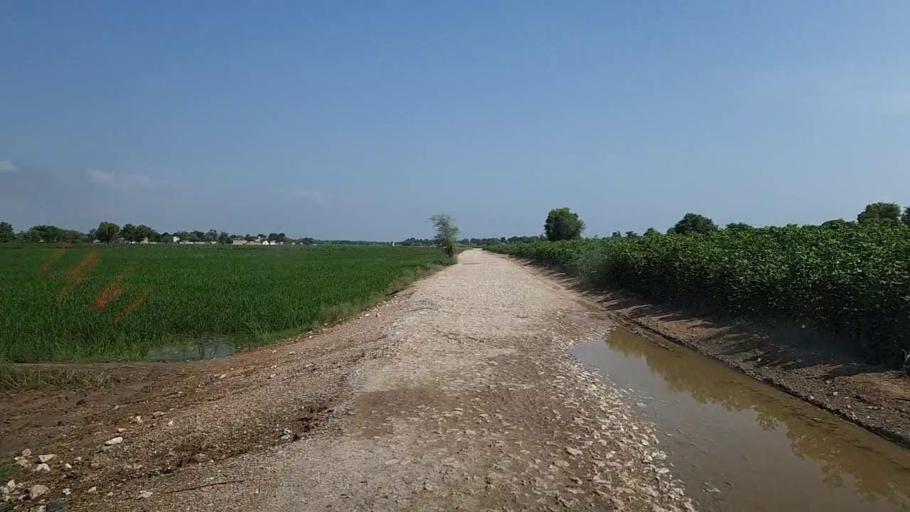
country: PK
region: Sindh
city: Bhiria
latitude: 26.8770
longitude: 68.2305
